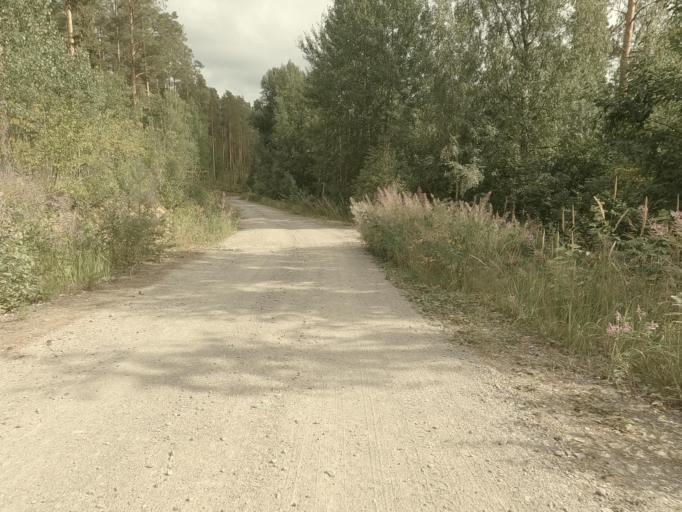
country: RU
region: Leningrad
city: Kamennogorsk
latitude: 60.9754
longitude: 29.1745
